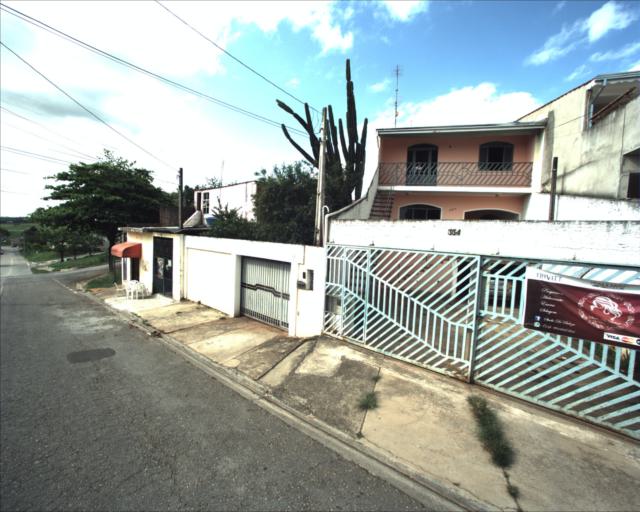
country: BR
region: Sao Paulo
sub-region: Sorocaba
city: Sorocaba
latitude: -23.3966
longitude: -47.3806
